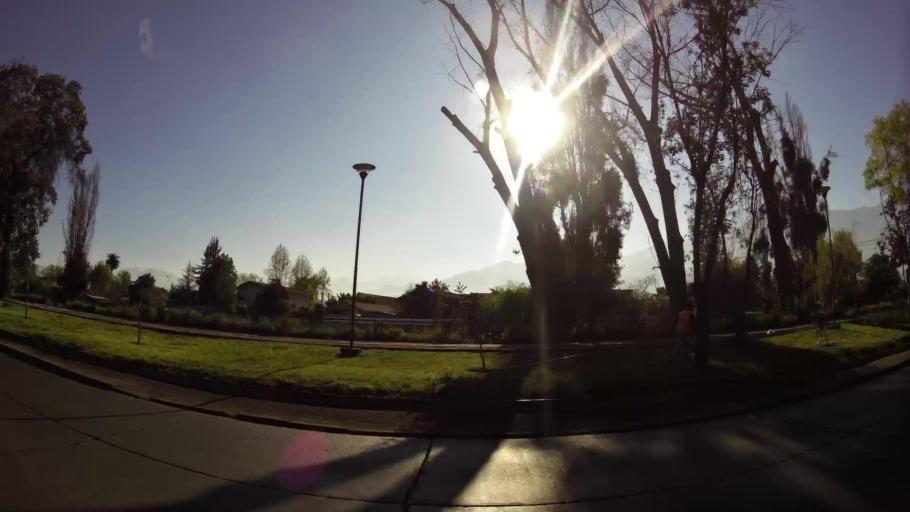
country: CL
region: Santiago Metropolitan
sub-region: Provincia de Santiago
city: Villa Presidente Frei, Nunoa, Santiago, Chile
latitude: -33.4541
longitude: -70.5576
